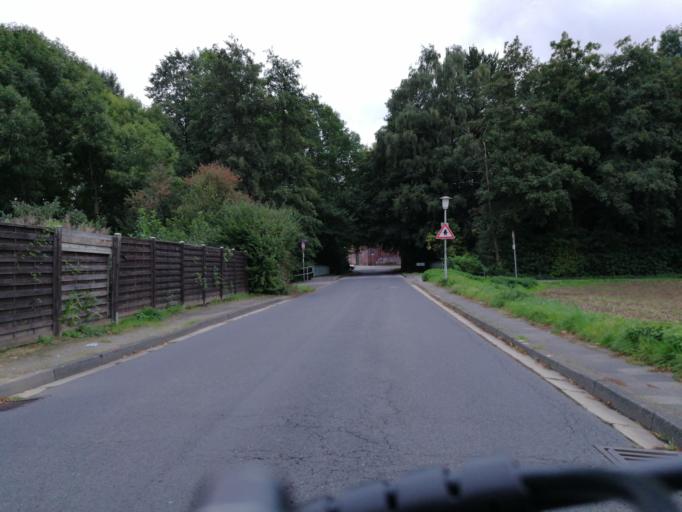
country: DE
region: North Rhine-Westphalia
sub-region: Regierungsbezirk Dusseldorf
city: Neuss
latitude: 51.1350
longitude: 6.7362
